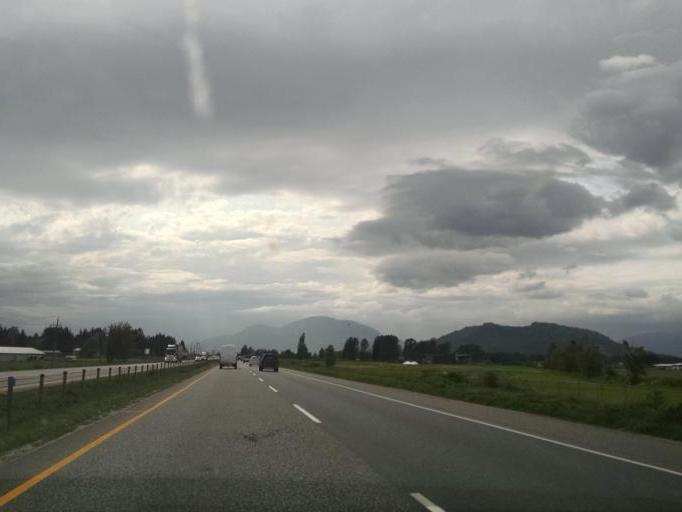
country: CA
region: British Columbia
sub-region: Fraser Valley Regional District
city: Chilliwack
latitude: 49.1514
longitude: -121.9357
